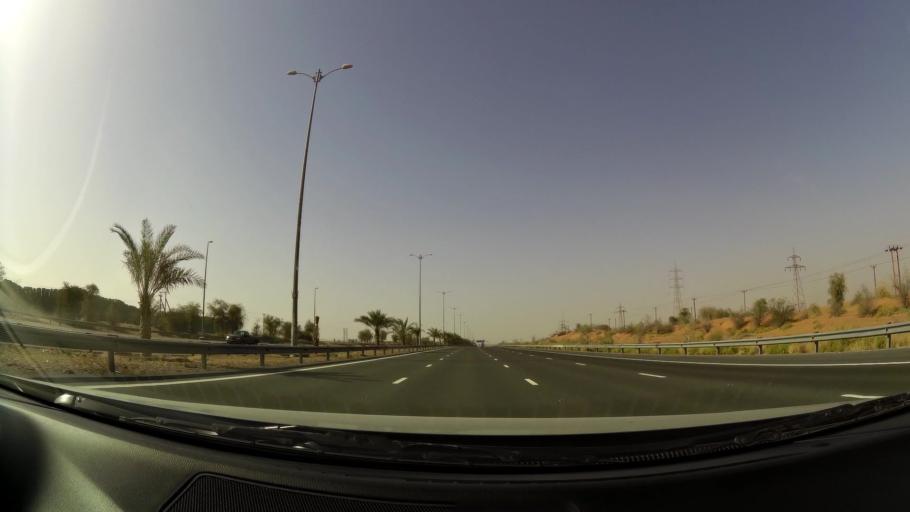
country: OM
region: Al Buraimi
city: Al Buraymi
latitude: 24.4489
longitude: 55.7839
